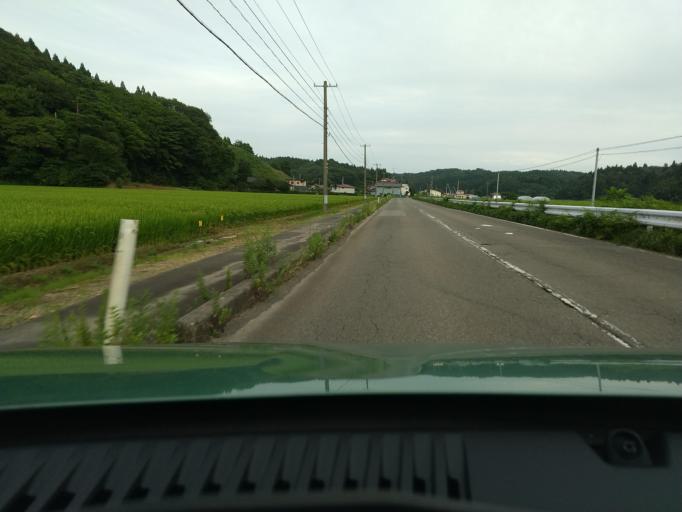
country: JP
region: Akita
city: Akita
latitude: 39.7843
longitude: 140.1258
